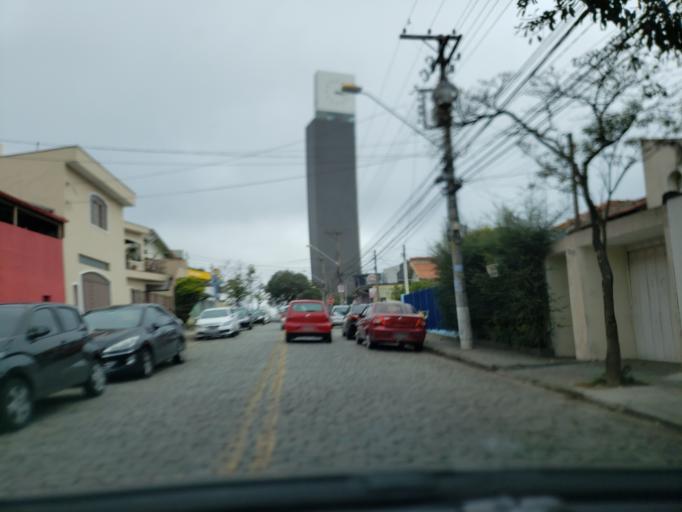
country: BR
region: Sao Paulo
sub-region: Santo Andre
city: Santo Andre
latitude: -23.6425
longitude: -46.5295
